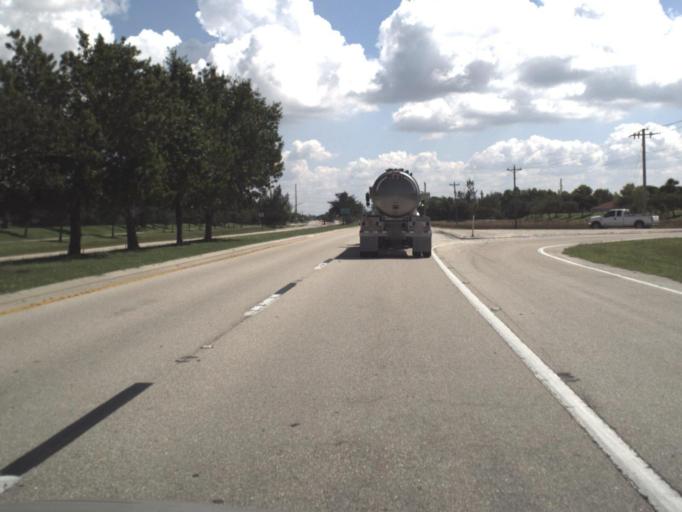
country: US
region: Florida
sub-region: Lee County
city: Cape Coral
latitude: 26.6071
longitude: -82.0201
